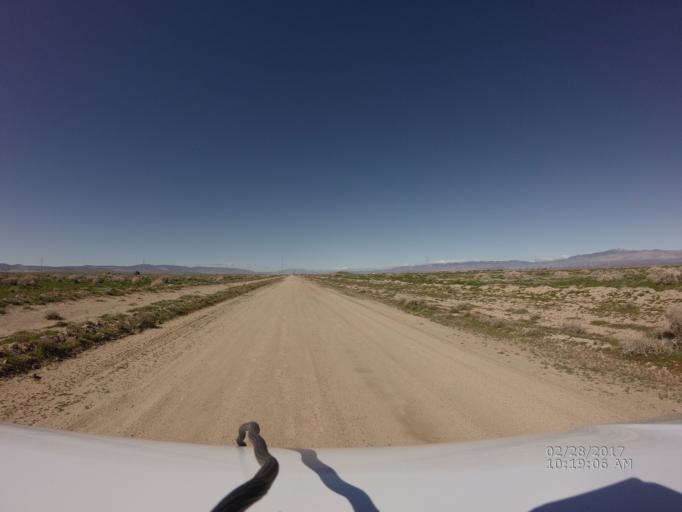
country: US
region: California
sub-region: Kern County
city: Rosamond
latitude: 34.7909
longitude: -118.3091
